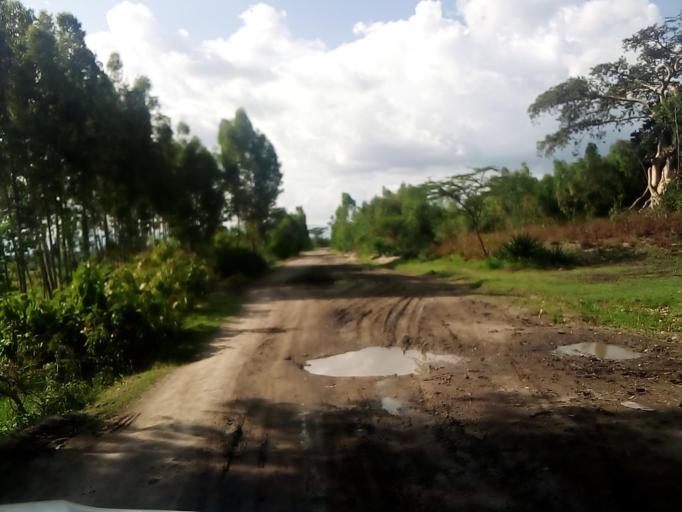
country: ET
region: Southern Nations, Nationalities, and People's Region
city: K'olito
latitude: 7.6535
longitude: 38.0496
